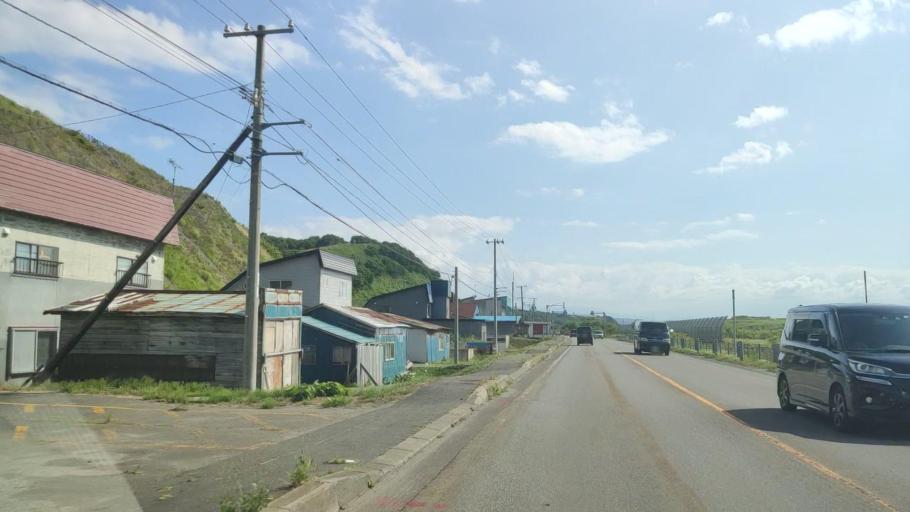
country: JP
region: Hokkaido
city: Rumoi
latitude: 43.9765
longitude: 141.6466
